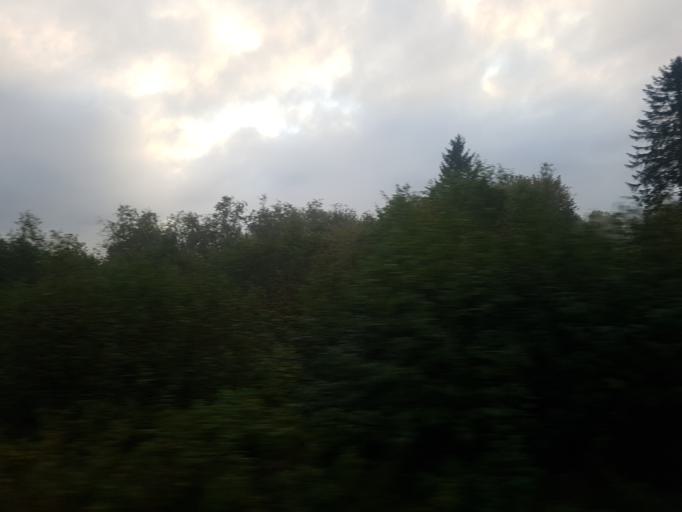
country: NO
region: Sor-Trondelag
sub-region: Melhus
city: Melhus
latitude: 63.3141
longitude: 10.2969
